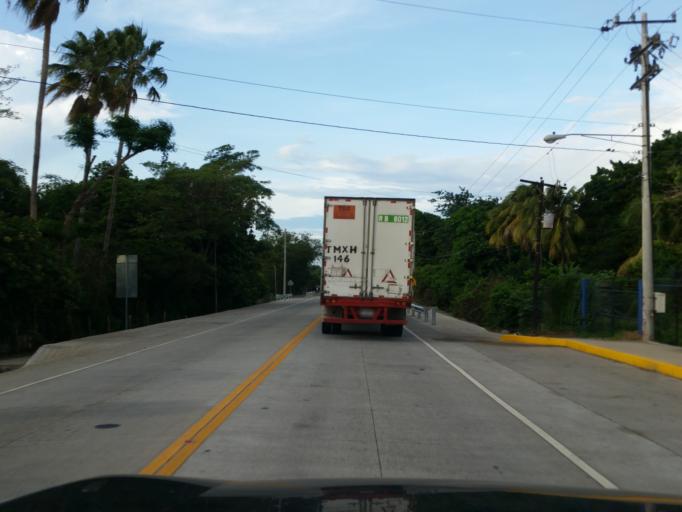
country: NI
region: Managua
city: Ciudad Sandino
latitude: 12.0893
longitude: -86.3562
